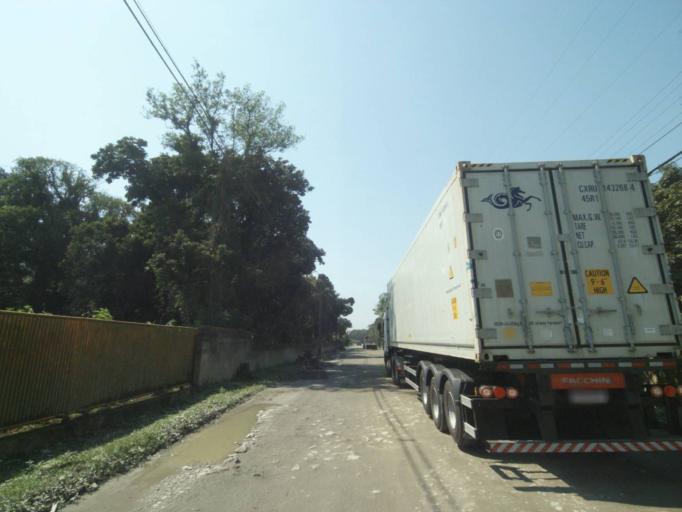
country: BR
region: Parana
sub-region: Paranagua
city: Paranagua
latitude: -25.5493
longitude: -48.5779
